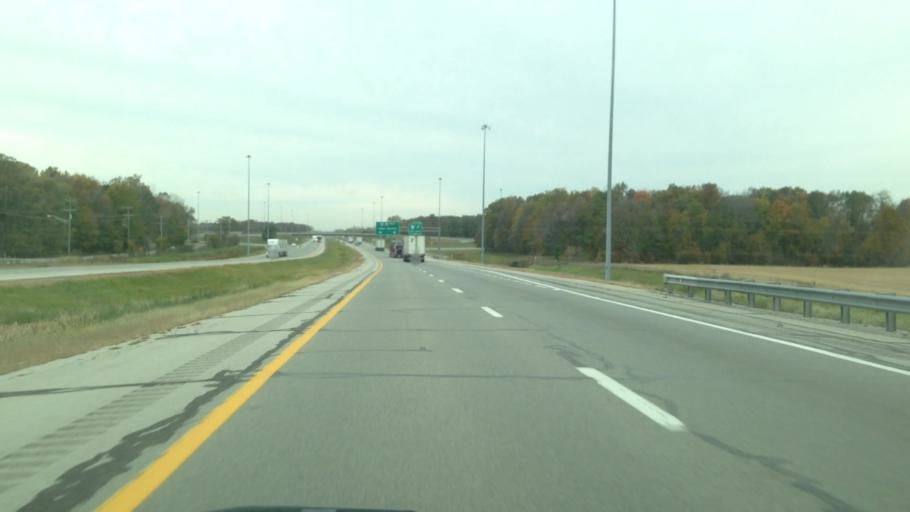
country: US
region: Ohio
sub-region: Williams County
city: Pioneer
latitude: 41.6133
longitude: -84.5412
